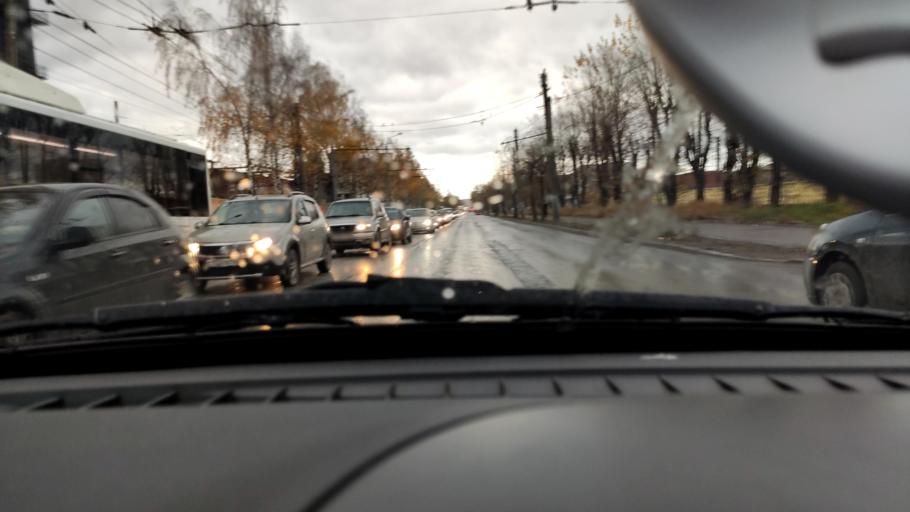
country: RU
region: Perm
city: Perm
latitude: 57.9803
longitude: 56.2467
